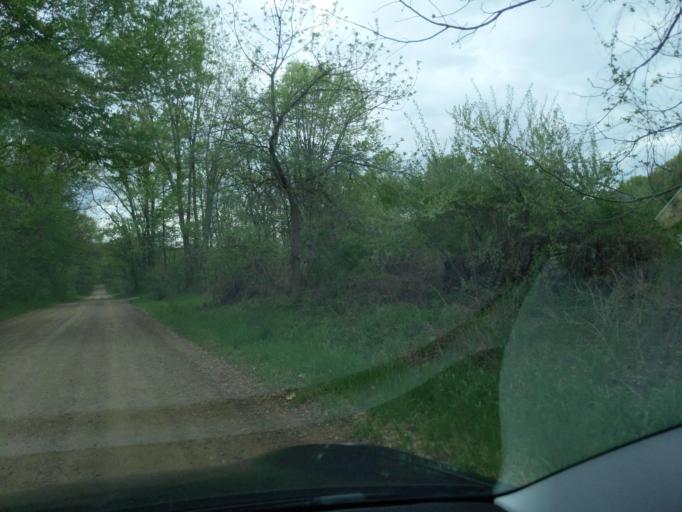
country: US
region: Michigan
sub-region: Ingham County
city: Stockbridge
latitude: 42.5172
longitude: -84.2884
